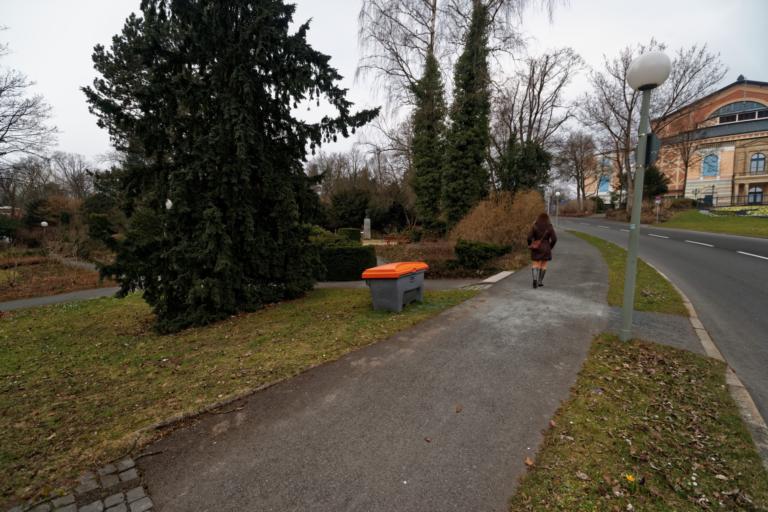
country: DE
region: Bavaria
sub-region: Upper Franconia
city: Bayreuth
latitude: 49.9587
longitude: 11.5792
